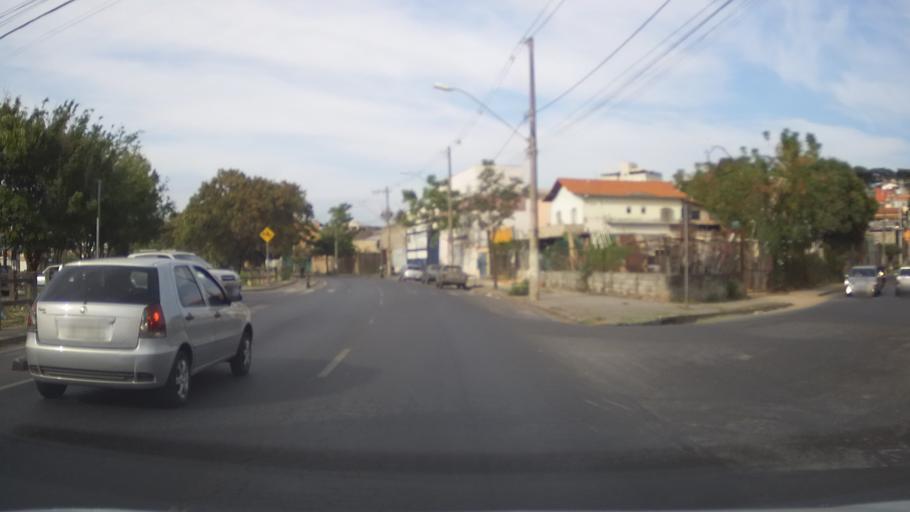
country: BR
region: Minas Gerais
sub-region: Contagem
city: Contagem
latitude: -19.8683
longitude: -44.0110
